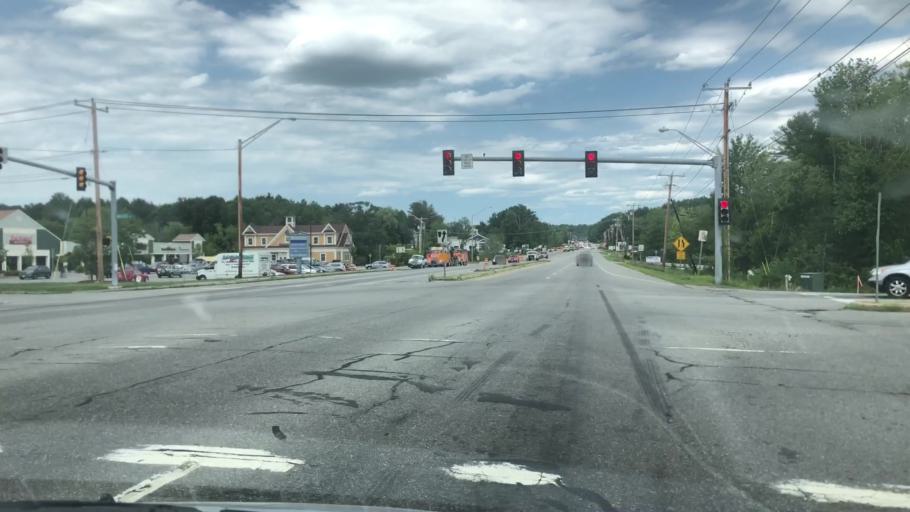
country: US
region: New Hampshire
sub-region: Hillsborough County
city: Bedford
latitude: 42.9374
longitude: -71.5263
